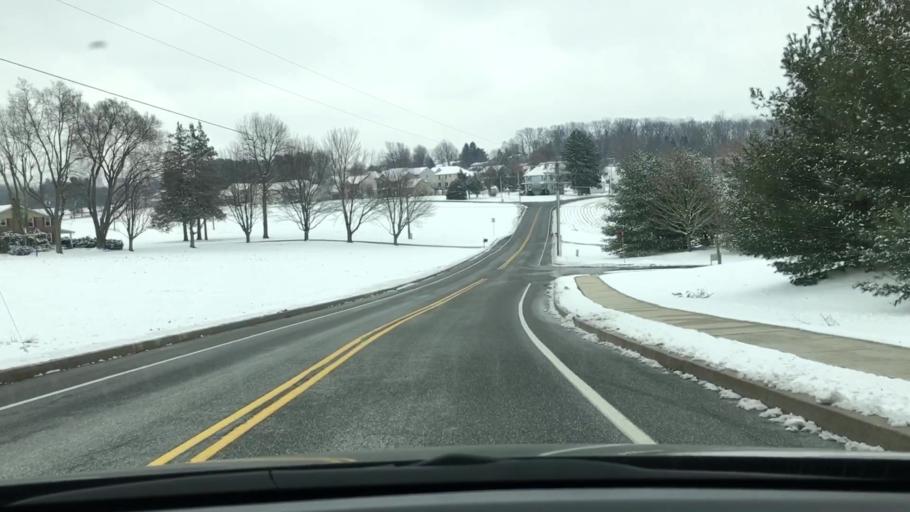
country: US
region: Pennsylvania
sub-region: York County
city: Spry
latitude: 39.9140
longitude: -76.6703
